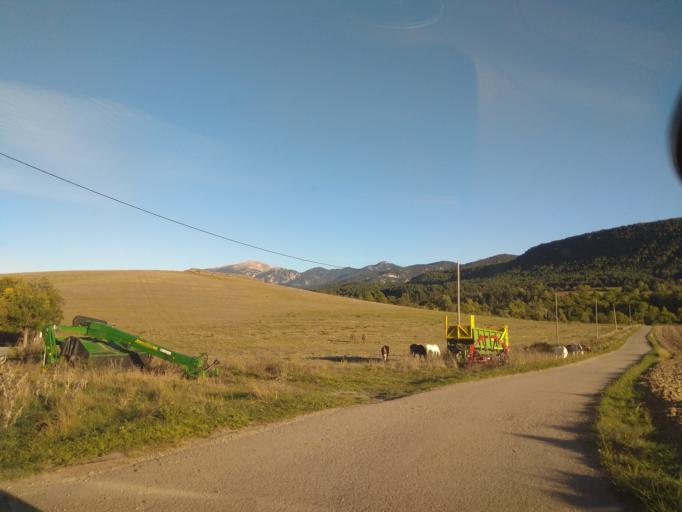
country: ES
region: Catalonia
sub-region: Provincia de Lleida
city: Lles de Cerdanya
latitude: 42.3616
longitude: 1.7273
